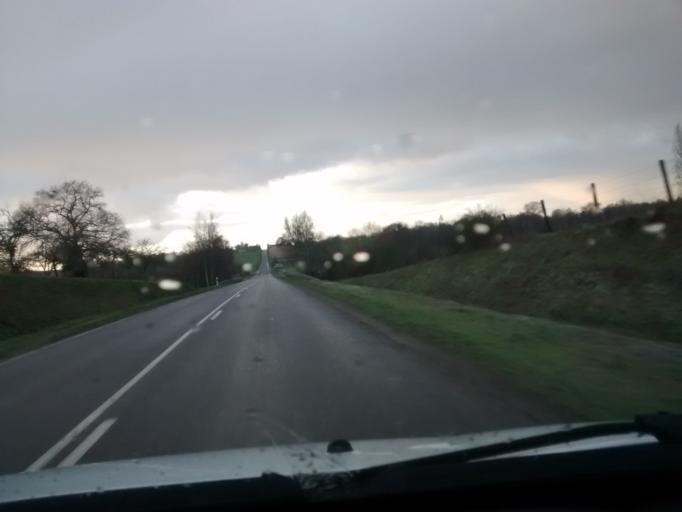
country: FR
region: Brittany
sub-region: Departement d'Ille-et-Vilaine
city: Bais
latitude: 47.9998
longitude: -1.2880
